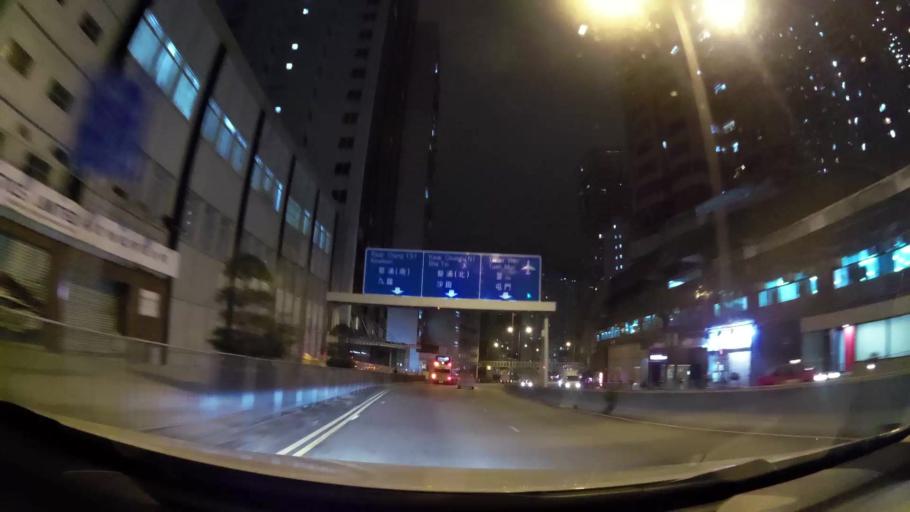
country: HK
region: Tsuen Wan
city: Tsuen Wan
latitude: 22.3655
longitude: 114.1352
